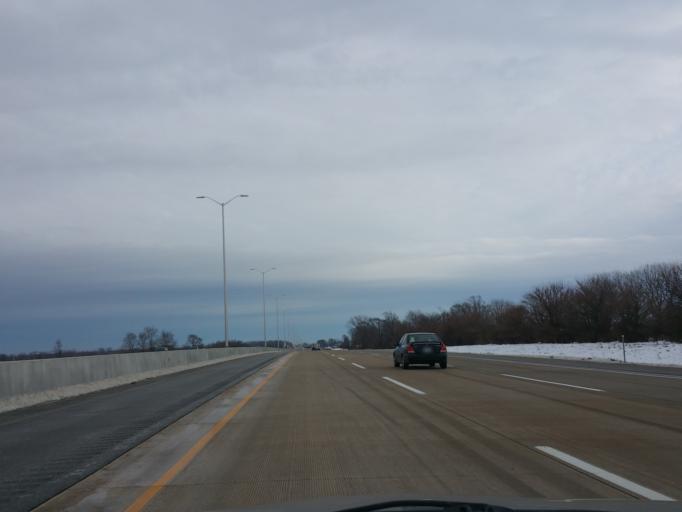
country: US
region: Illinois
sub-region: McHenry County
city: Marengo
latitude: 42.2059
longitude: -88.7032
